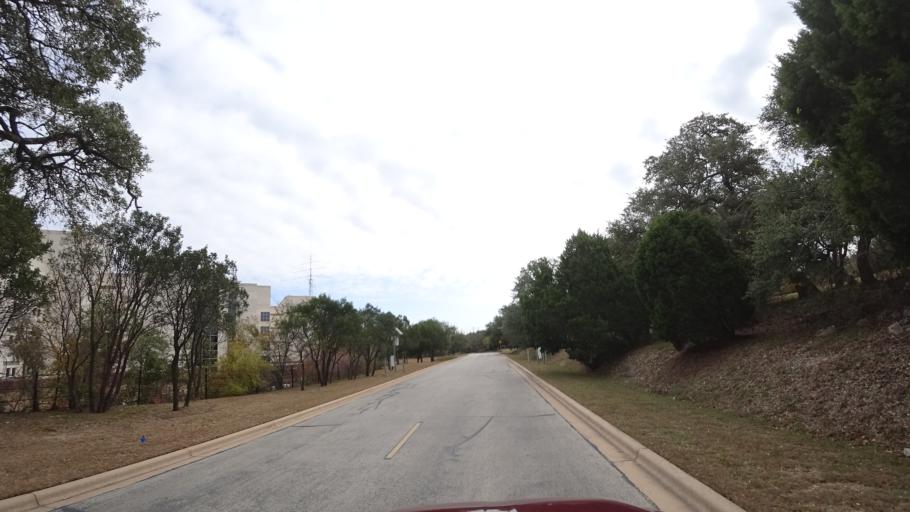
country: US
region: Texas
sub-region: Williamson County
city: Anderson Mill
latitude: 30.3931
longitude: -97.8408
